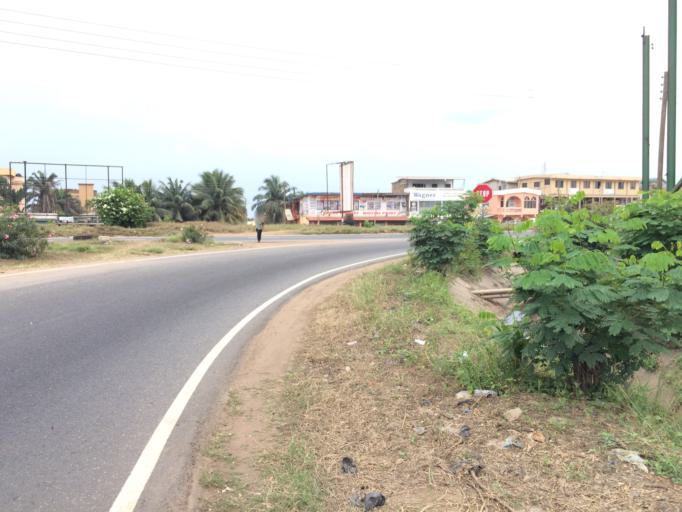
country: GH
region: Greater Accra
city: Accra
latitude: 5.5567
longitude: -0.1675
